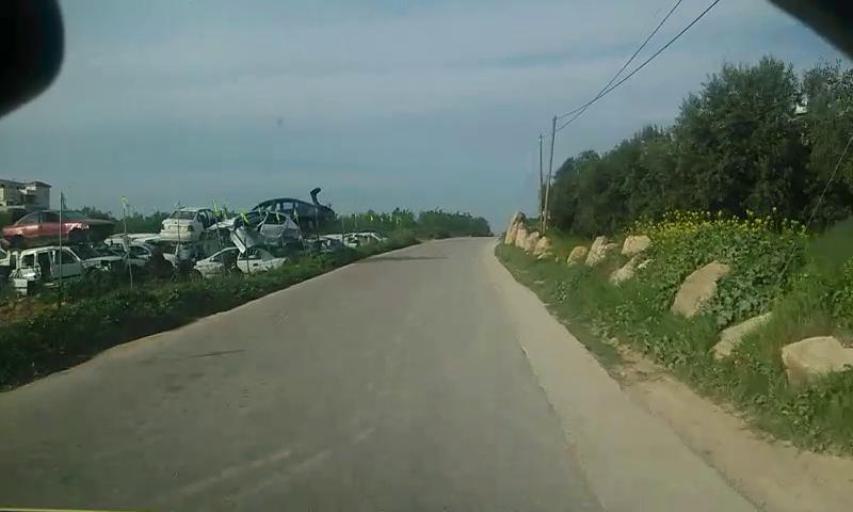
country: PS
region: West Bank
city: Bayt Ula
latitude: 31.6072
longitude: 35.0154
